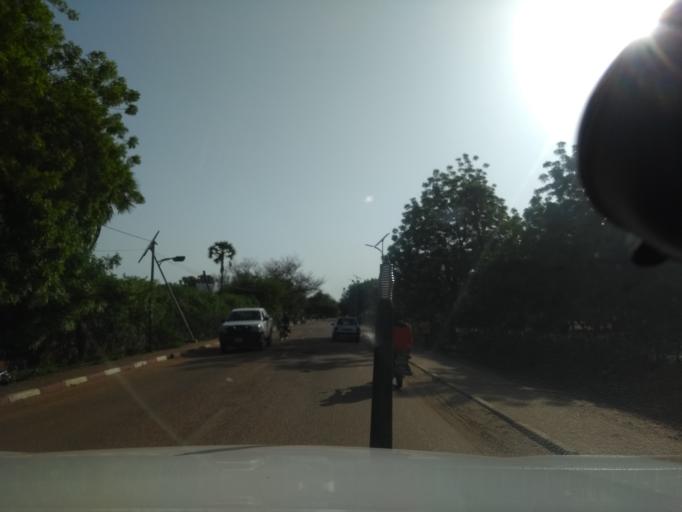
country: NE
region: Niamey
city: Niamey
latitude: 13.5012
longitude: 2.0958
